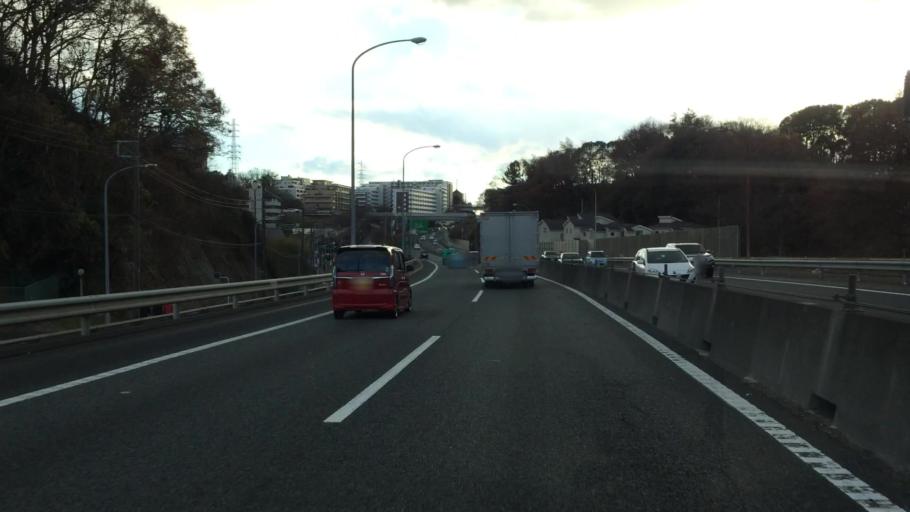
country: JP
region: Kanagawa
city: Yokohama
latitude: 35.4383
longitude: 139.5557
